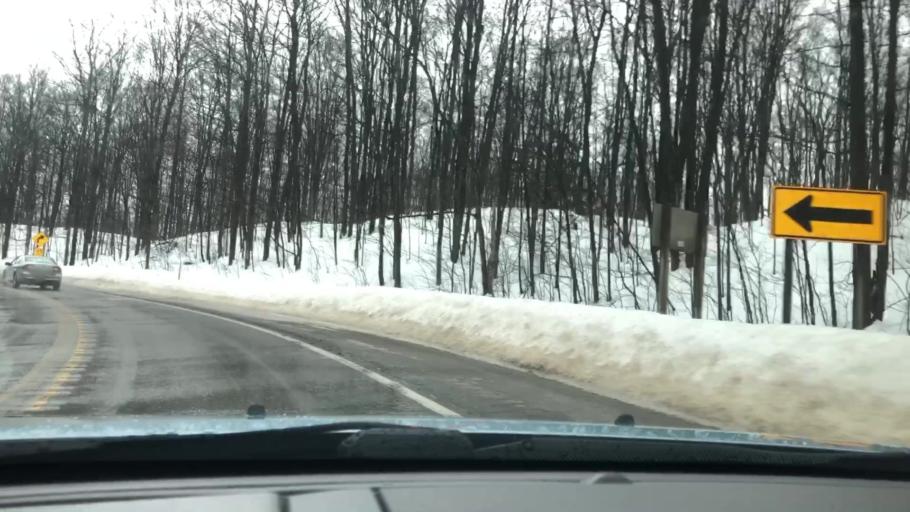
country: US
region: Michigan
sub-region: Charlevoix County
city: Boyne City
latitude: 45.0797
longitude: -84.9119
